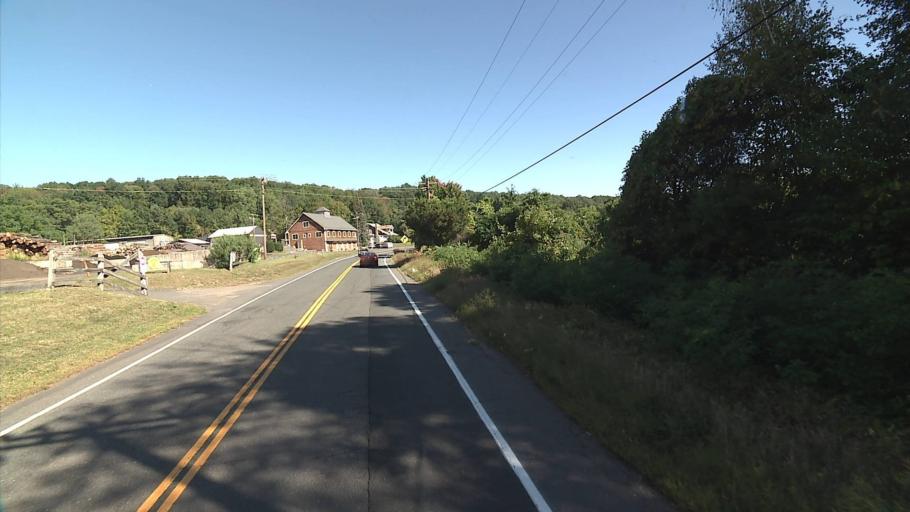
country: US
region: Connecticut
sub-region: Hartford County
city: Collinsville
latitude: 41.7604
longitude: -72.9756
